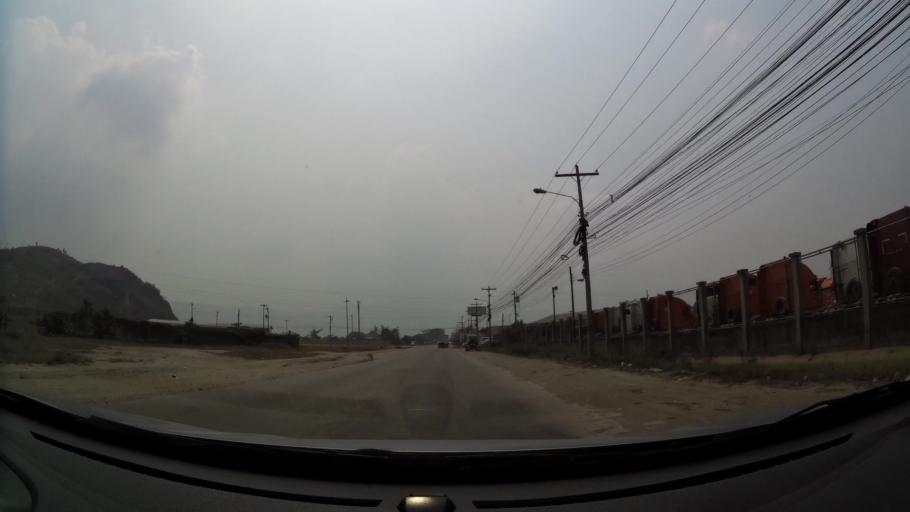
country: HN
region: Cortes
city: Chotepe
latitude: 15.4674
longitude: -87.9819
